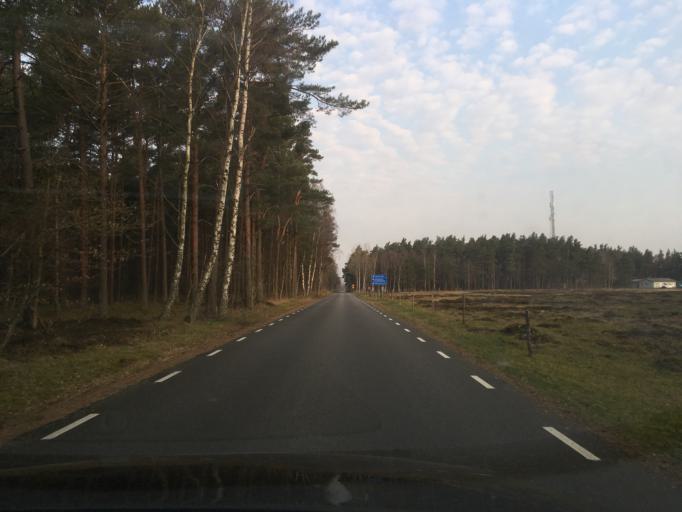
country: SE
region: Skane
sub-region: Simrishamns Kommun
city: Simrishamn
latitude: 55.3932
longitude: 14.1817
